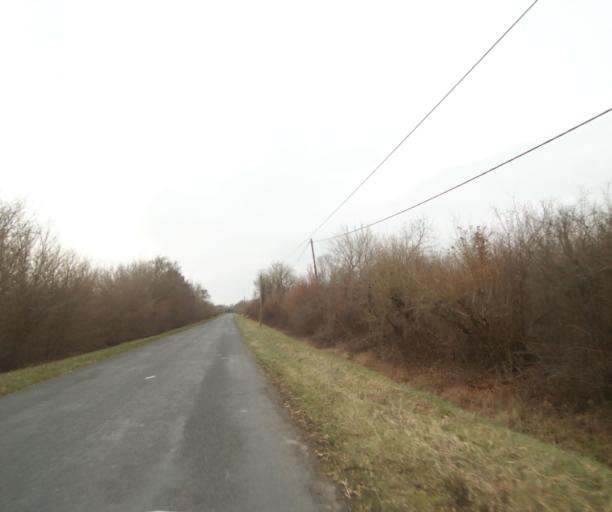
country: FR
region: Champagne-Ardenne
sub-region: Departement de la Haute-Marne
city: Villiers-en-Lieu
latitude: 48.6525
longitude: 4.8756
